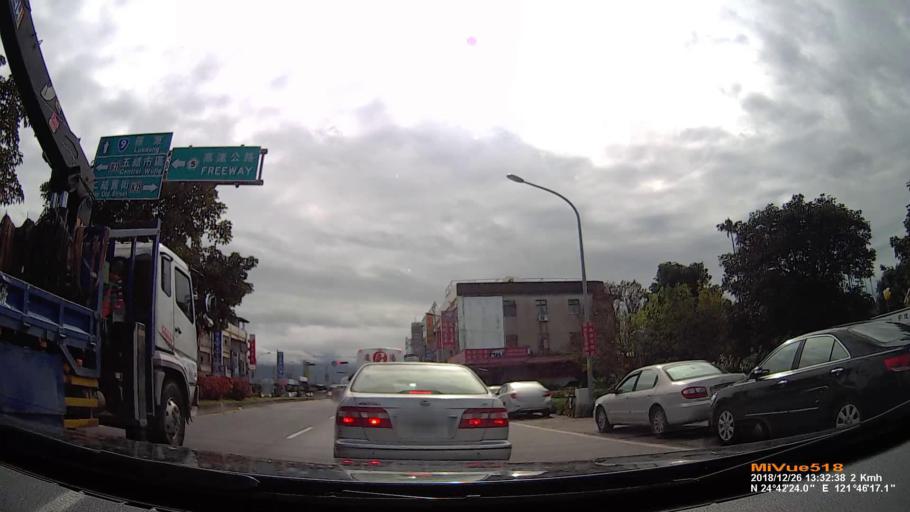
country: TW
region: Taiwan
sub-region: Yilan
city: Yilan
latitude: 24.6923
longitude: 121.7698
